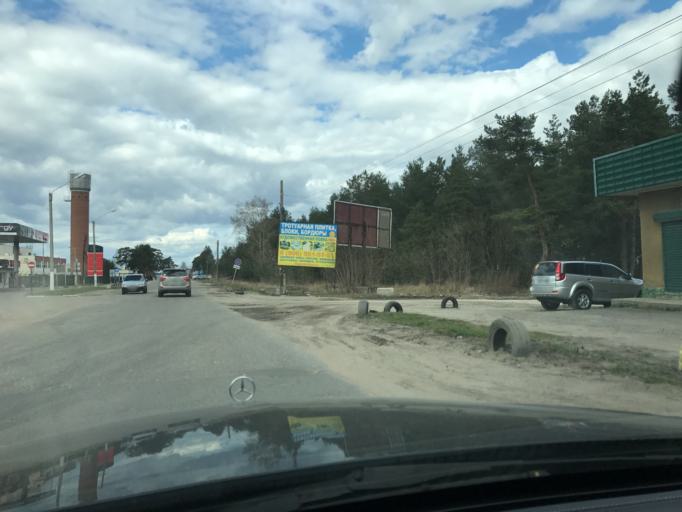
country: RU
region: Vladimir
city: Pokrov
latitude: 55.9011
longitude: 39.1968
